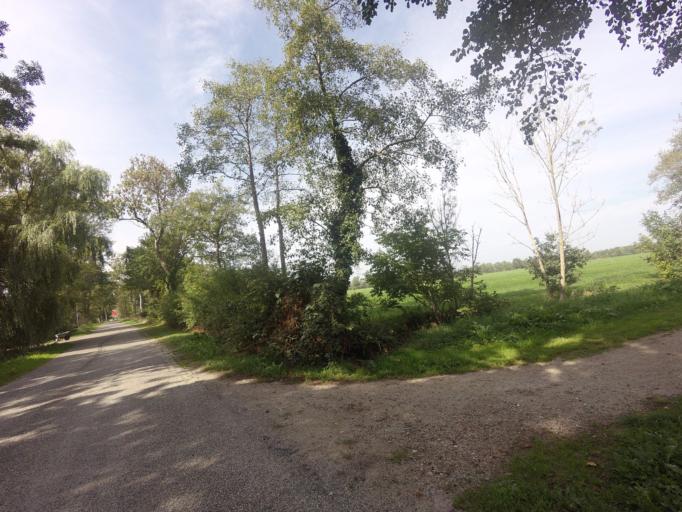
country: NL
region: Groningen
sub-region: Gemeente Zuidhorn
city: Grijpskerk
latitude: 53.2150
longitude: 6.3366
